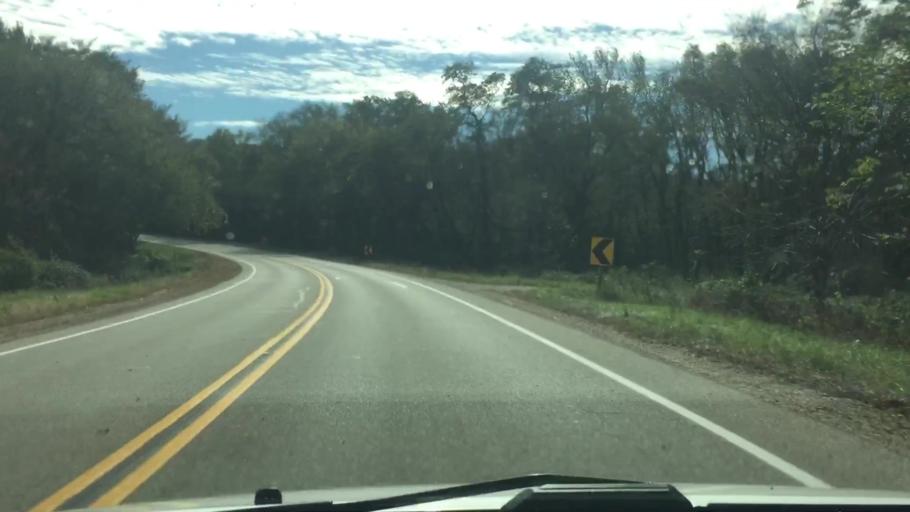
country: US
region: Wisconsin
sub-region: Waukesha County
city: Eagle
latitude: 42.9440
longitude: -88.4781
